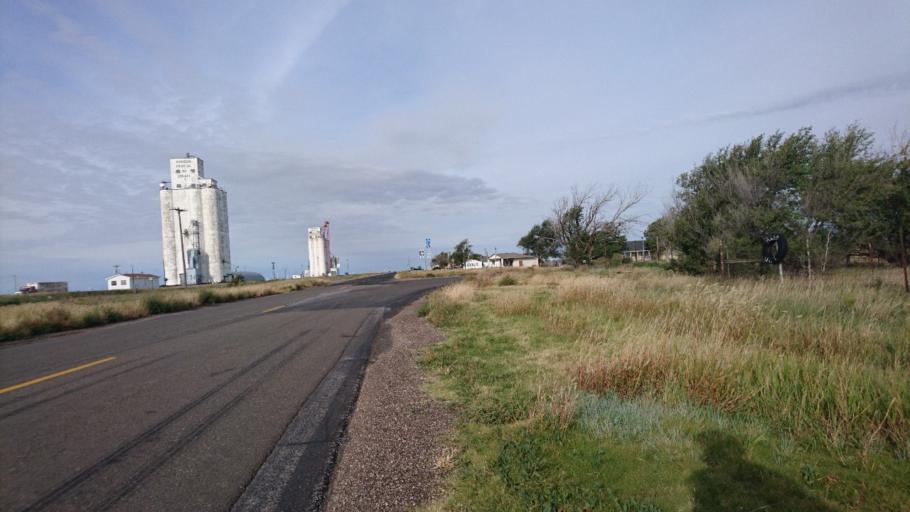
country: US
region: Texas
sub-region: Armstrong County
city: Claude
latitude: 35.2076
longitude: -101.3814
